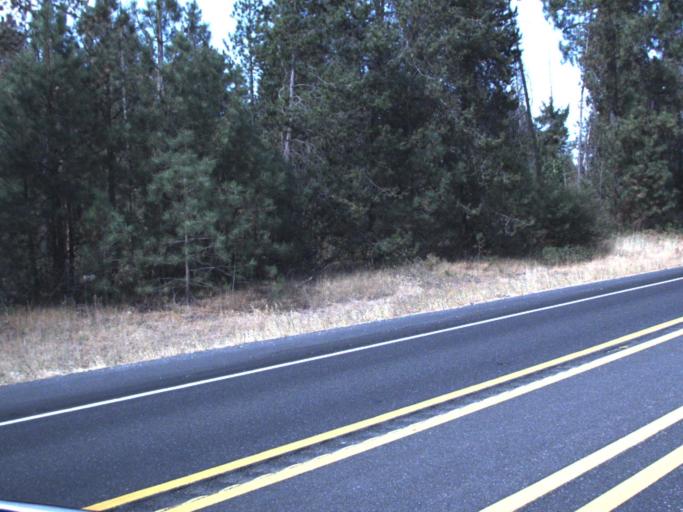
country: US
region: Washington
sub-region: Spokane County
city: Deer Park
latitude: 47.9461
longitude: -117.4806
